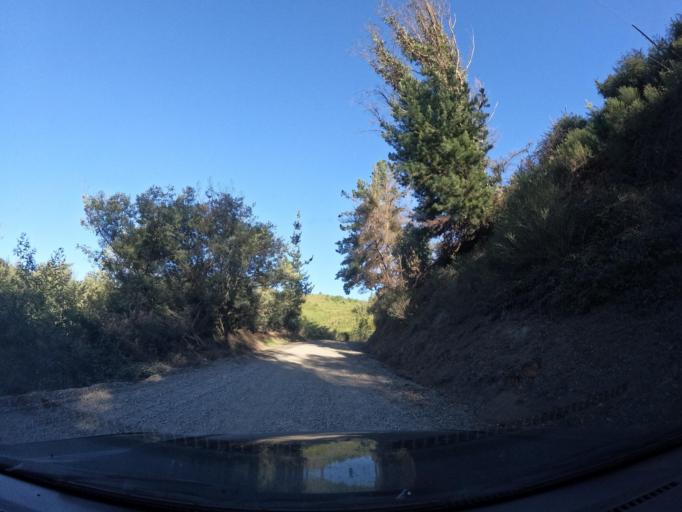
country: CL
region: Biobio
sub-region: Provincia de Concepcion
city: Chiguayante
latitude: -37.0144
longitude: -72.8925
